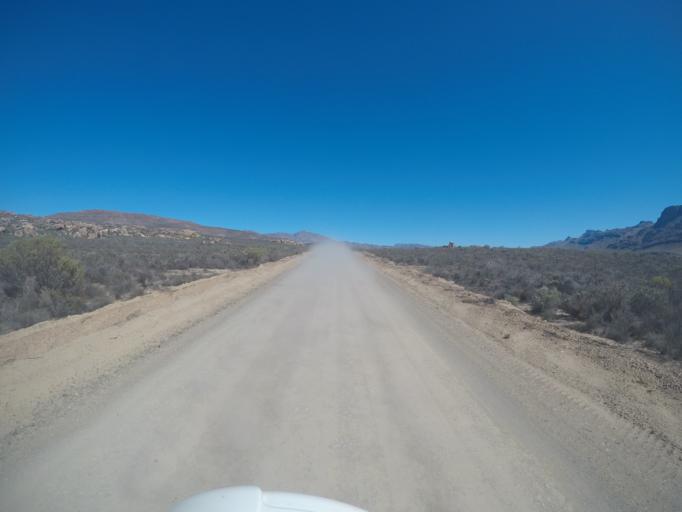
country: ZA
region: Western Cape
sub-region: West Coast District Municipality
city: Clanwilliam
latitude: -32.5053
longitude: 19.2920
